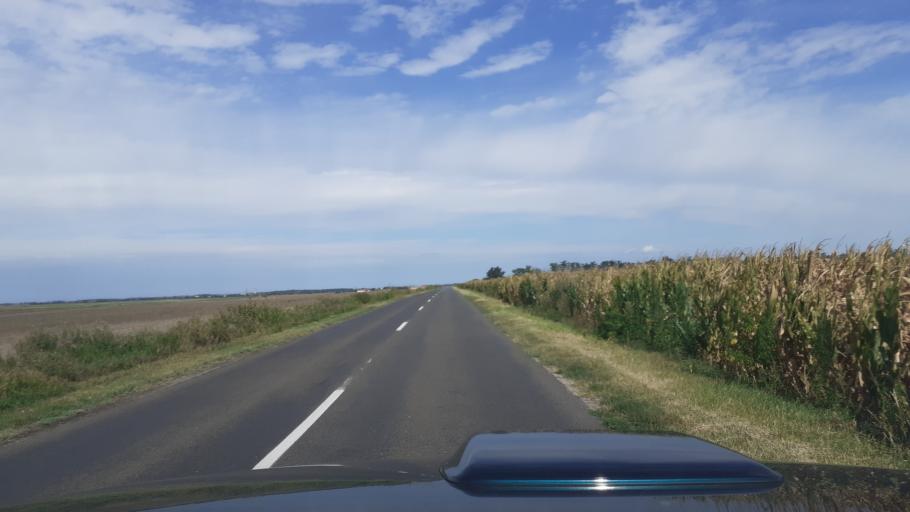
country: HU
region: Fejer
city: Pusztaszabolcs
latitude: 47.1008
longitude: 18.7130
